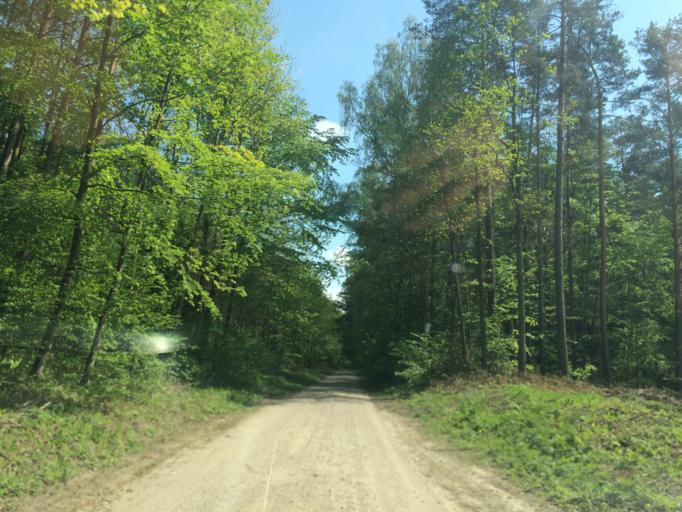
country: PL
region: Warmian-Masurian Voivodeship
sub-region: Powiat nowomiejski
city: Nowe Miasto Lubawskie
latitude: 53.4499
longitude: 19.6243
